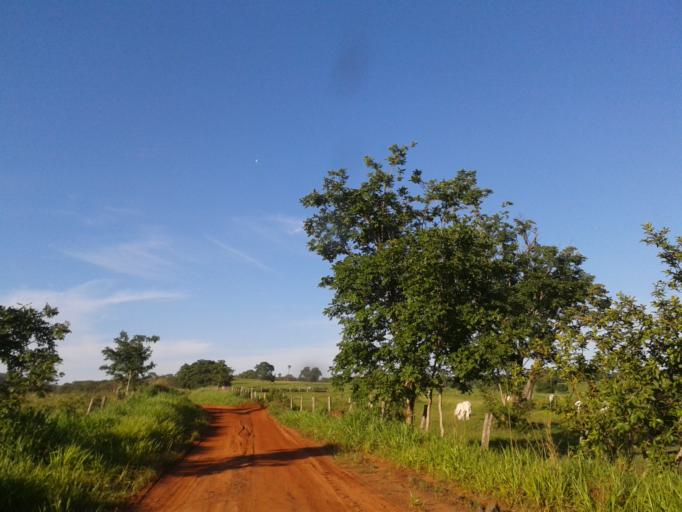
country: BR
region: Minas Gerais
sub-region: Santa Vitoria
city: Santa Vitoria
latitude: -18.9630
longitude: -49.8715
